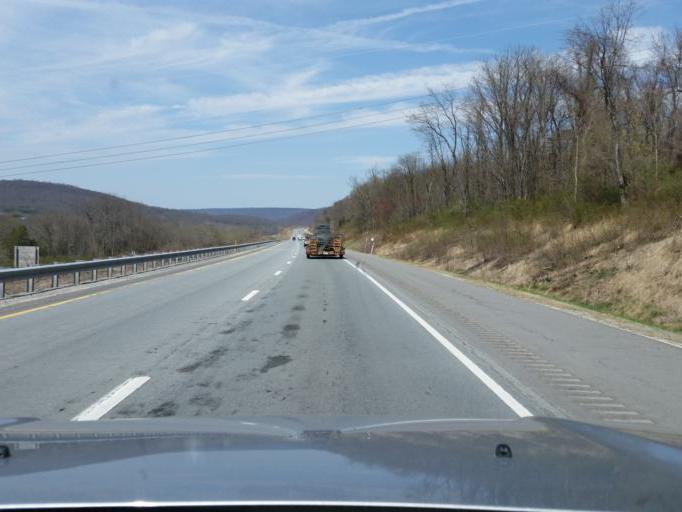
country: US
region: Pennsylvania
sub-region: Perry County
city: Duncannon
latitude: 40.4455
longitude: -77.0172
